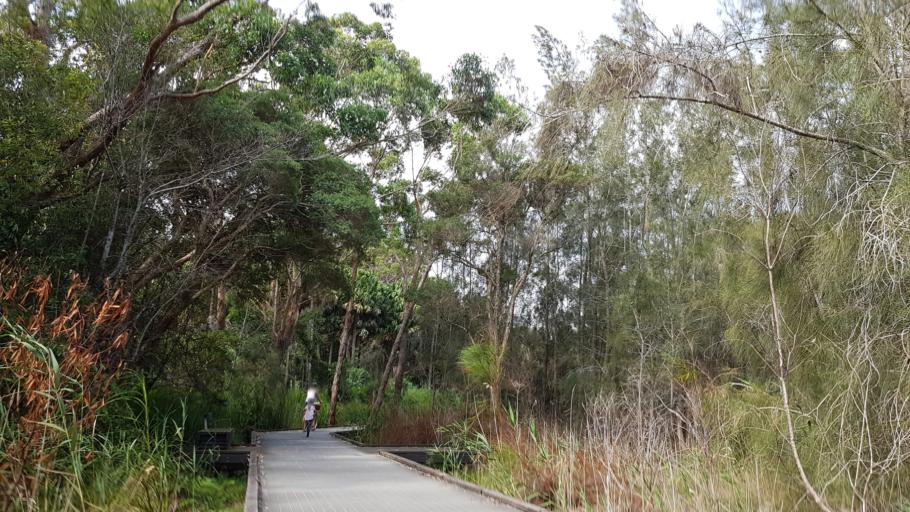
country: AU
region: New South Wales
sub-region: Pittwater
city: North Narrabeen
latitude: -33.7135
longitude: 151.2703
